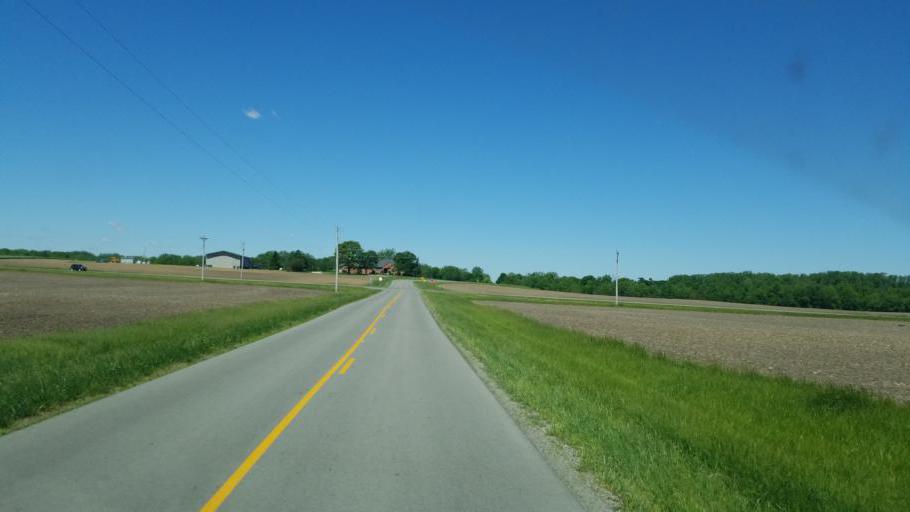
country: US
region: Ohio
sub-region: Logan County
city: Russells Point
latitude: 40.4194
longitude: -83.9077
